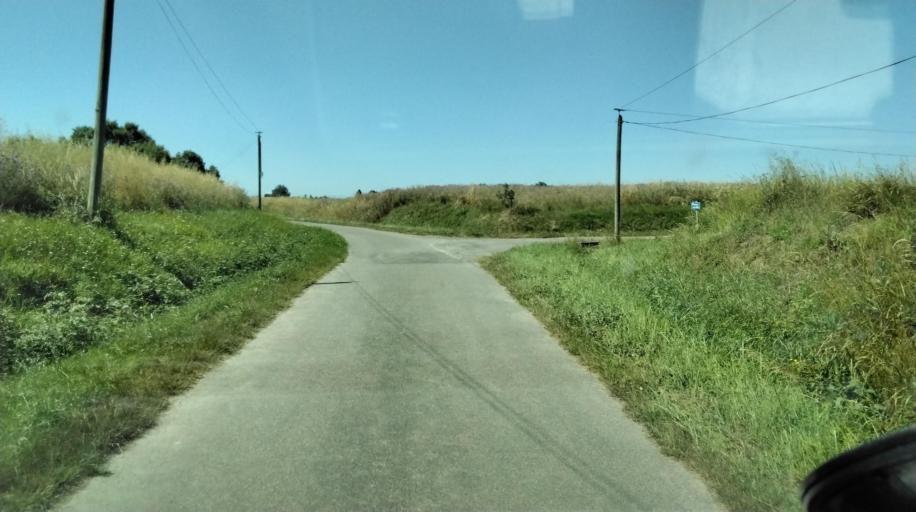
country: FR
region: Midi-Pyrenees
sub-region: Departement de la Haute-Garonne
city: Sainte-Foy-de-Peyrolieres
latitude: 43.4844
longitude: 1.1317
